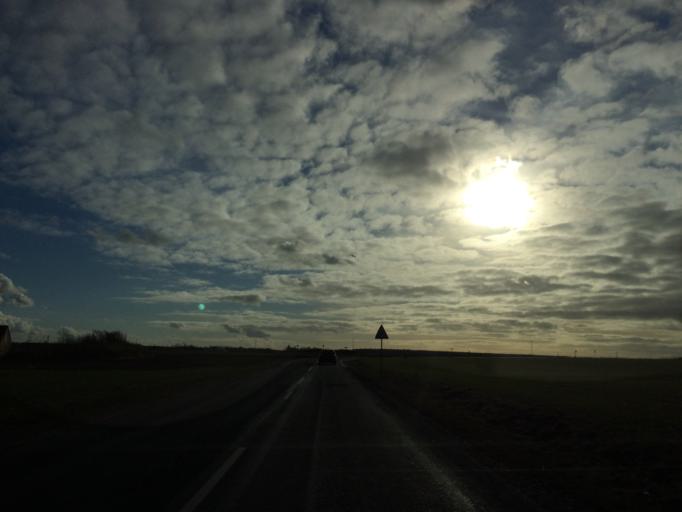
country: DK
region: Central Jutland
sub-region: Lemvig Kommune
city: Lemvig
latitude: 56.5225
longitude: 8.3547
